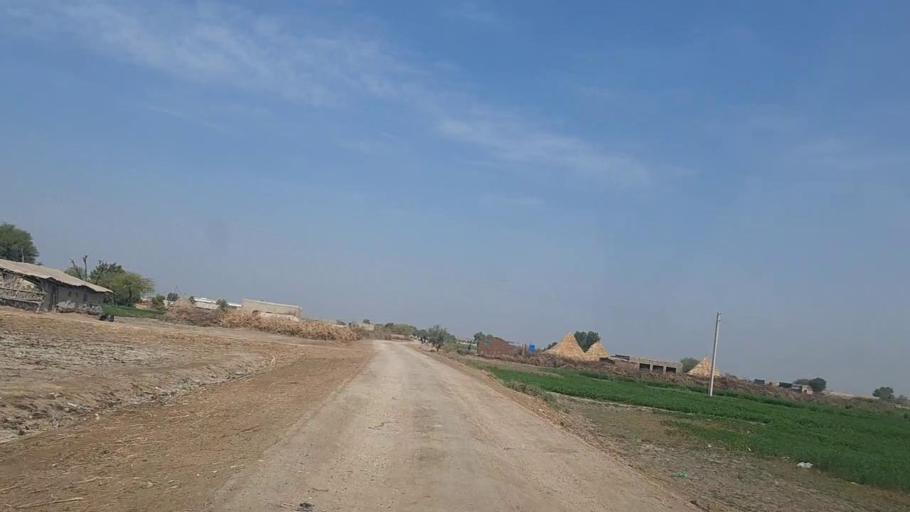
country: PK
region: Sindh
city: Mirpur Khas
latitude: 25.5022
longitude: 68.9209
